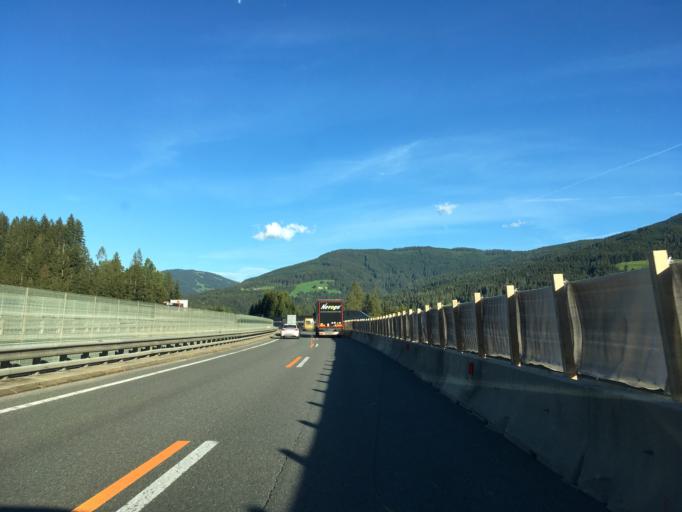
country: AT
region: Salzburg
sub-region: Politischer Bezirk Sankt Johann im Pongau
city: Huttau
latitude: 47.4192
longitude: 13.3114
